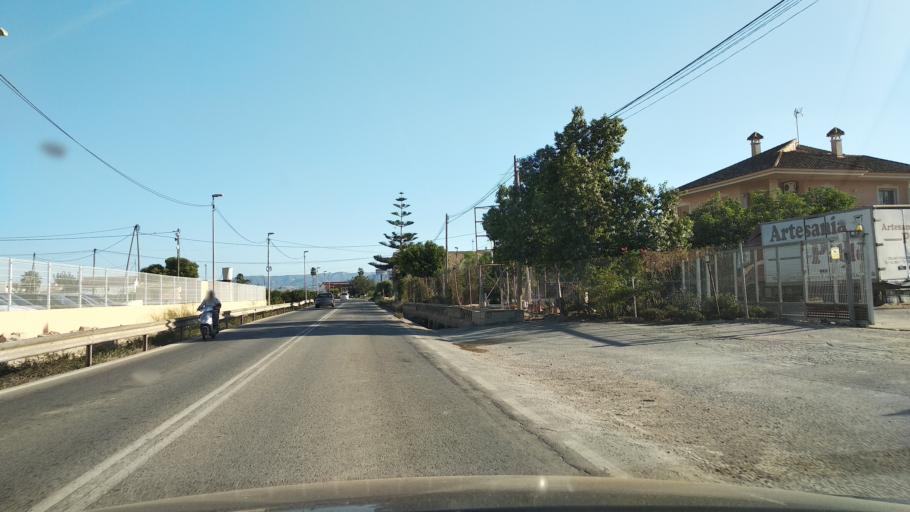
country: ES
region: Murcia
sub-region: Murcia
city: Santomera
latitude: 38.0471
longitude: -1.0543
